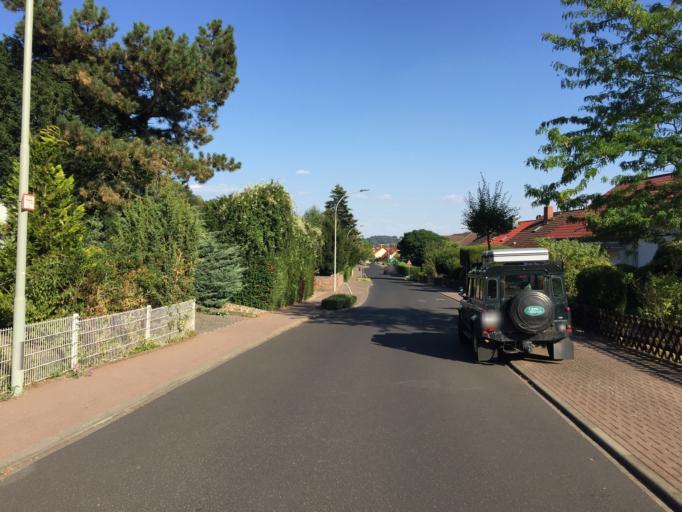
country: DE
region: Hesse
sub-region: Regierungsbezirk Giessen
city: Hoernsheim
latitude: 50.5419
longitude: 8.6640
